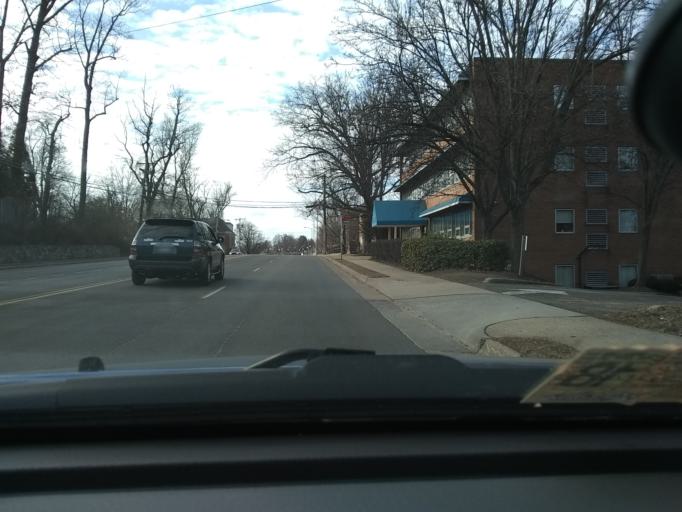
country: US
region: Virginia
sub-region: Fairfax County
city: Seven Corners
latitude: 38.8964
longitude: -77.1340
